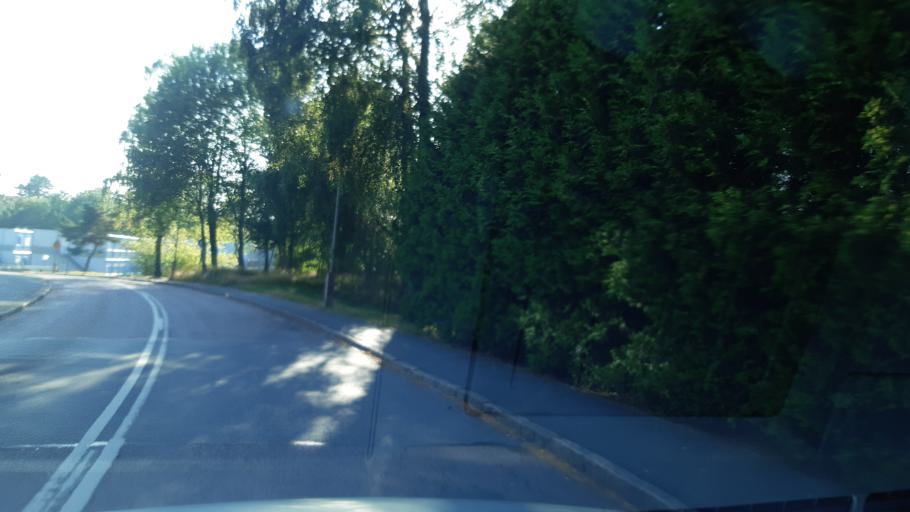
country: SE
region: Vaestra Goetaland
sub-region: Goteborg
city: Eriksbo
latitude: 57.7156
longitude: 12.0519
